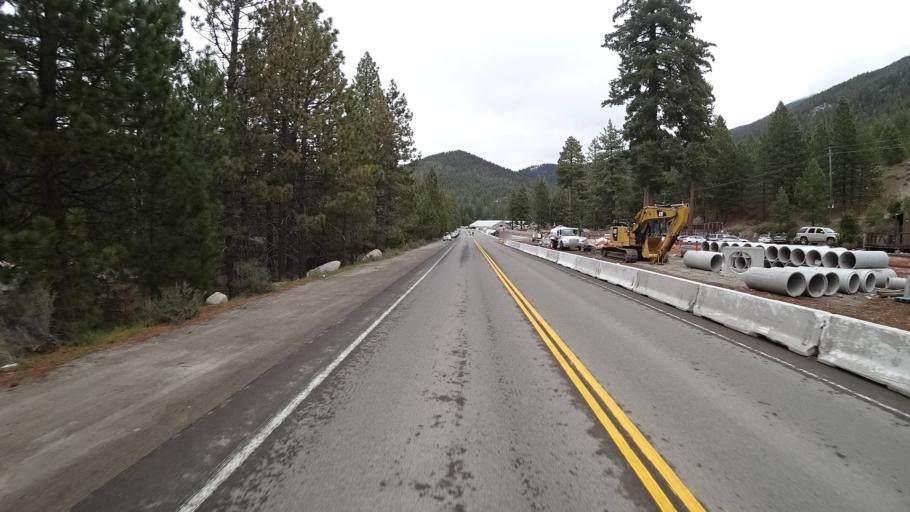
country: US
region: Nevada
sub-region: Washoe County
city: Incline Village
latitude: 39.2344
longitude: -119.9306
